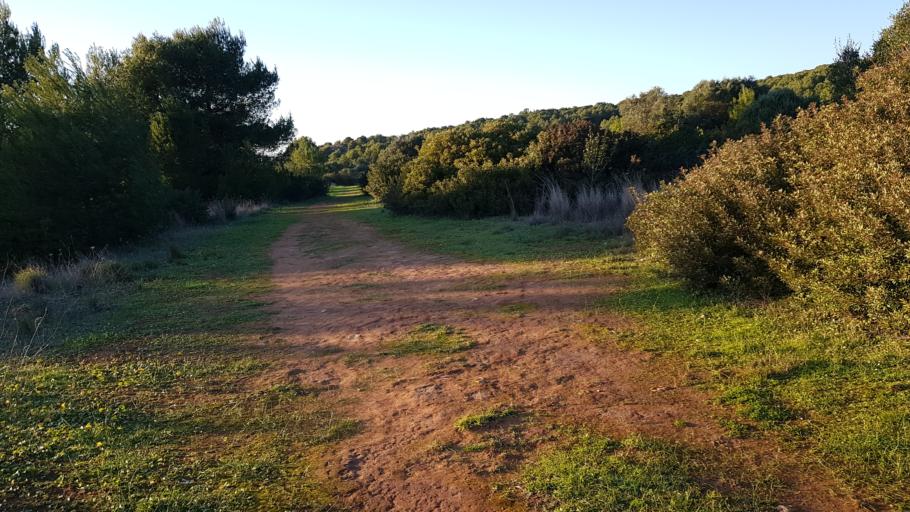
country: IT
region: Apulia
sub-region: Provincia di Lecce
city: Nardo
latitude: 40.1513
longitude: 17.9663
